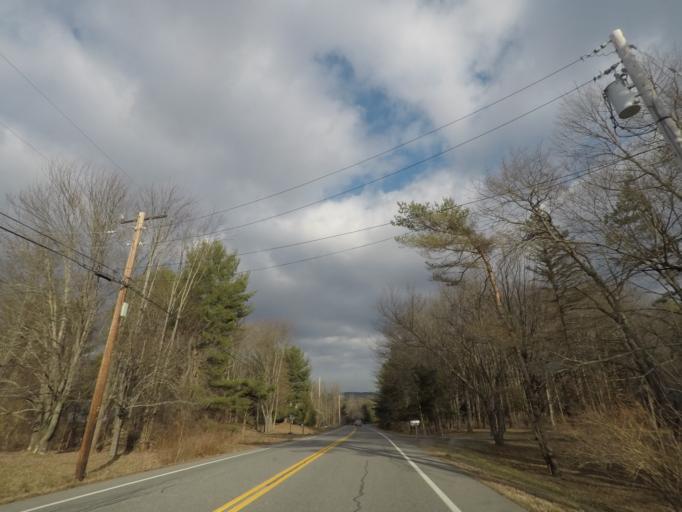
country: US
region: New York
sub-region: Albany County
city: Voorheesville
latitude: 42.6637
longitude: -73.9047
